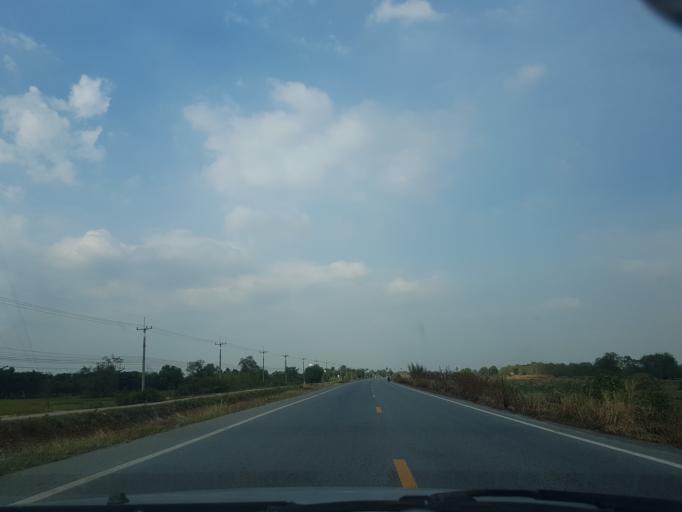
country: TH
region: Sara Buri
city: Nong Saeng
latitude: 14.5077
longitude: 100.7350
